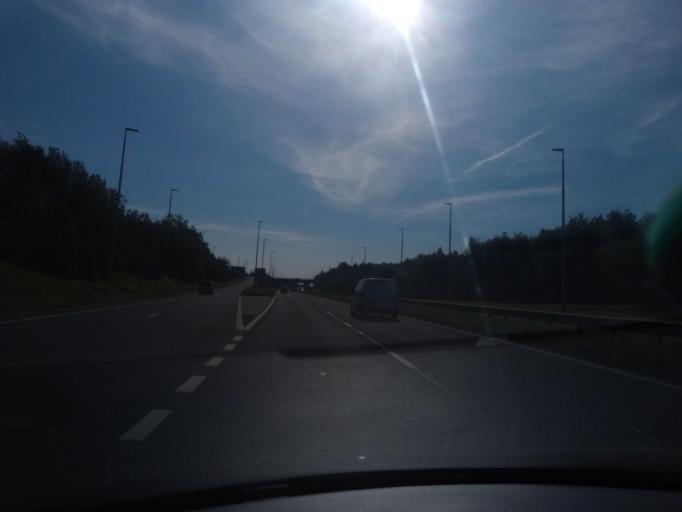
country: GB
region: England
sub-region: County Durham
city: Hawthorn
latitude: 54.8027
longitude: -1.3610
